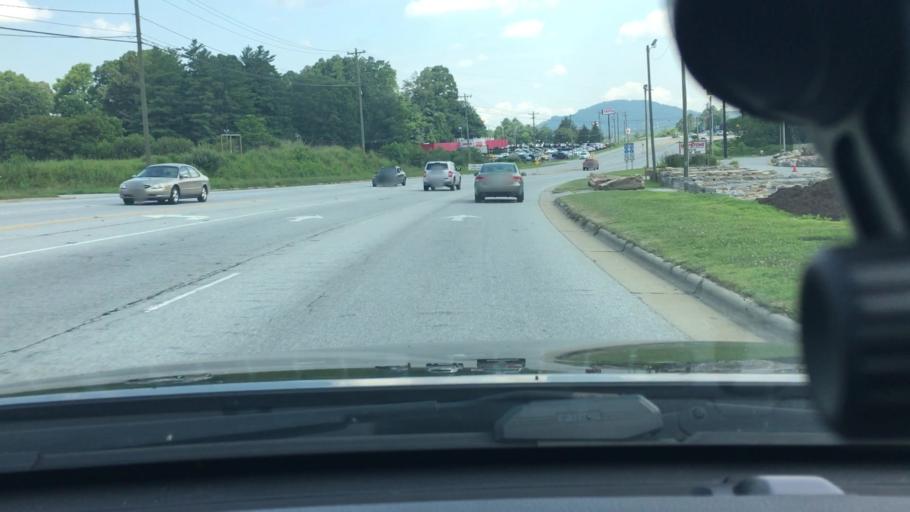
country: US
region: North Carolina
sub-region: Henderson County
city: Fletcher
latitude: 35.4032
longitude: -82.5099
